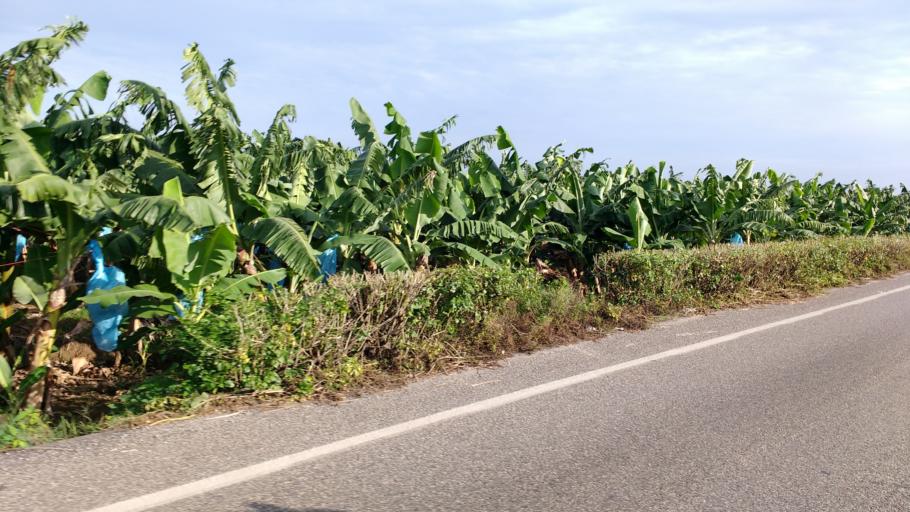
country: MX
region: Tabasco
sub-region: Teapa
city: Eureka y Belen
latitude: 17.6123
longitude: -92.9649
